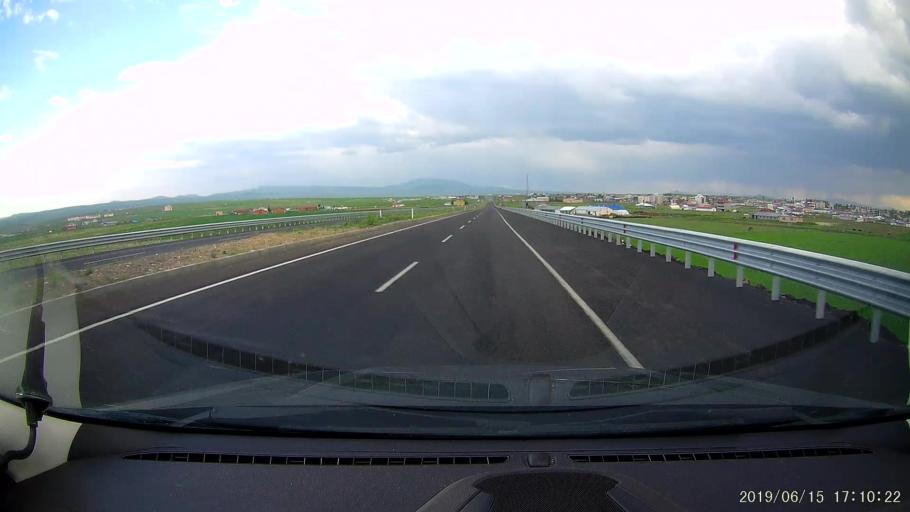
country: TR
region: Kars
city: Kars
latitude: 40.6229
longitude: 43.1338
